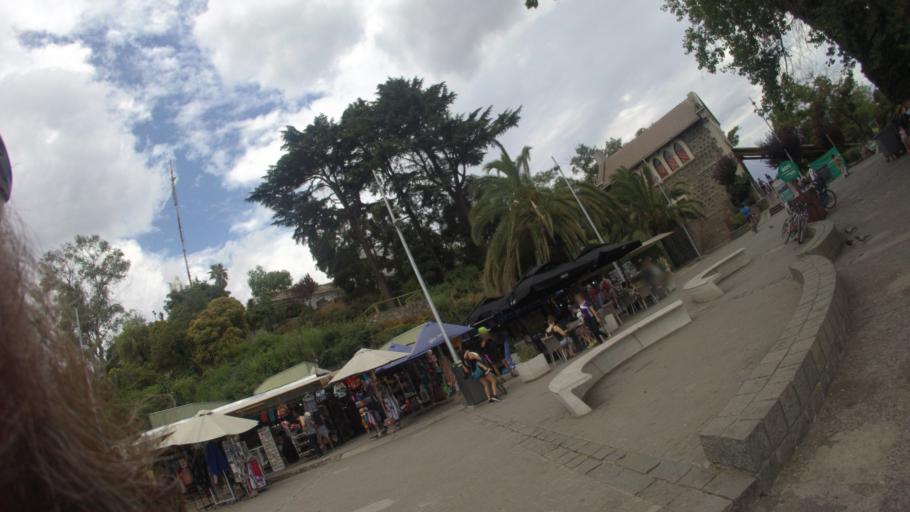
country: CL
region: Santiago Metropolitan
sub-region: Provincia de Santiago
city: Santiago
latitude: -33.4263
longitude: -70.6341
